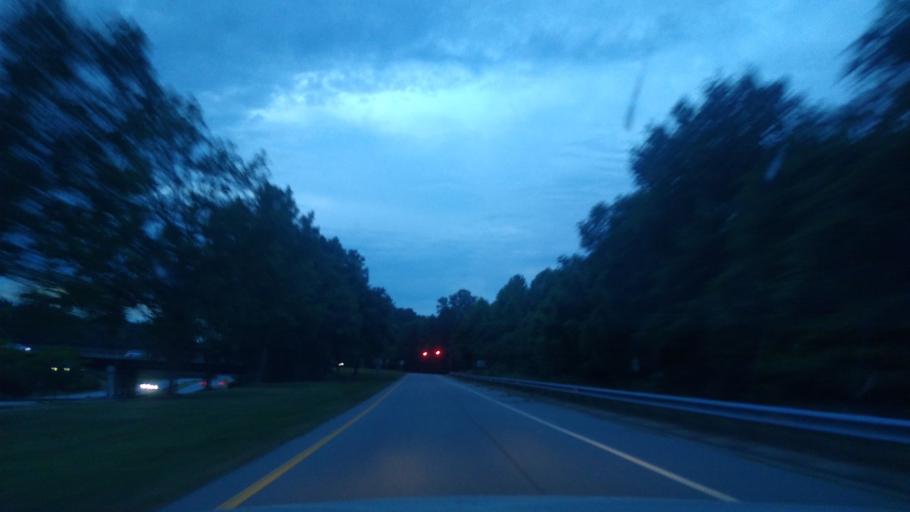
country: US
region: North Carolina
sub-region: Guilford County
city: Greensboro
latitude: 36.1031
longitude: -79.8371
